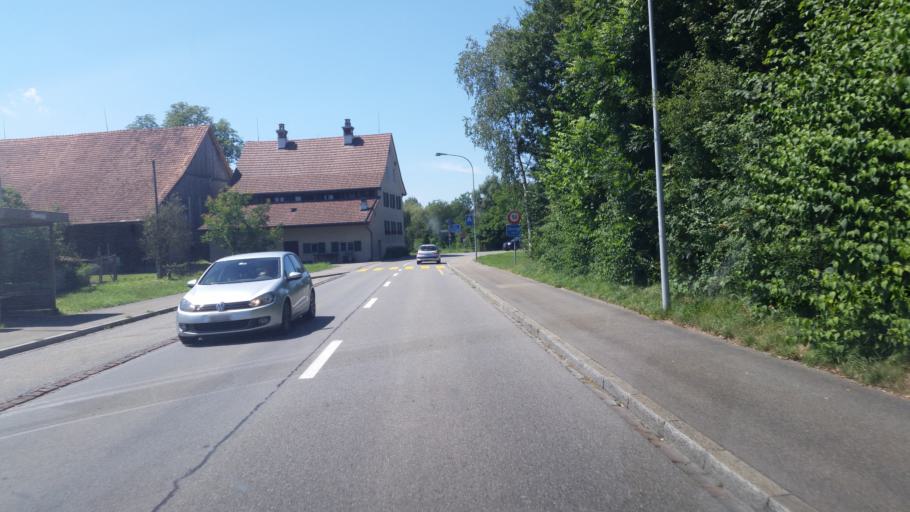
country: CH
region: Zurich
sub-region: Bezirk Buelach
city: End-Hoeri
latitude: 47.5041
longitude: 8.5006
